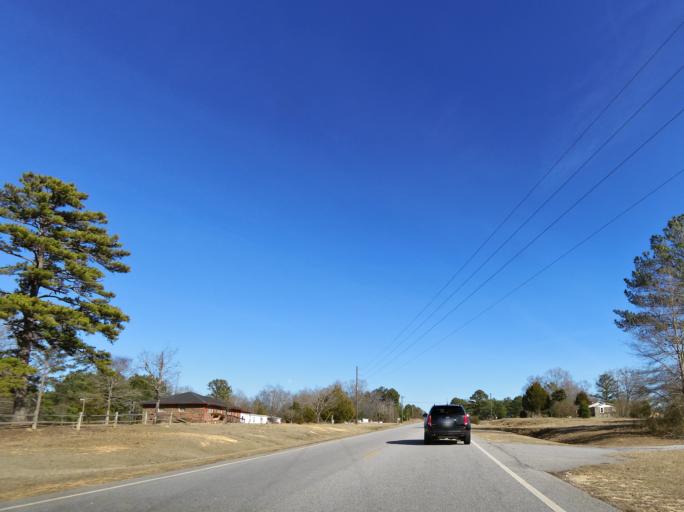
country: US
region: Georgia
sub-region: Crawford County
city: Roberta
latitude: 32.7524
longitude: -84.1807
